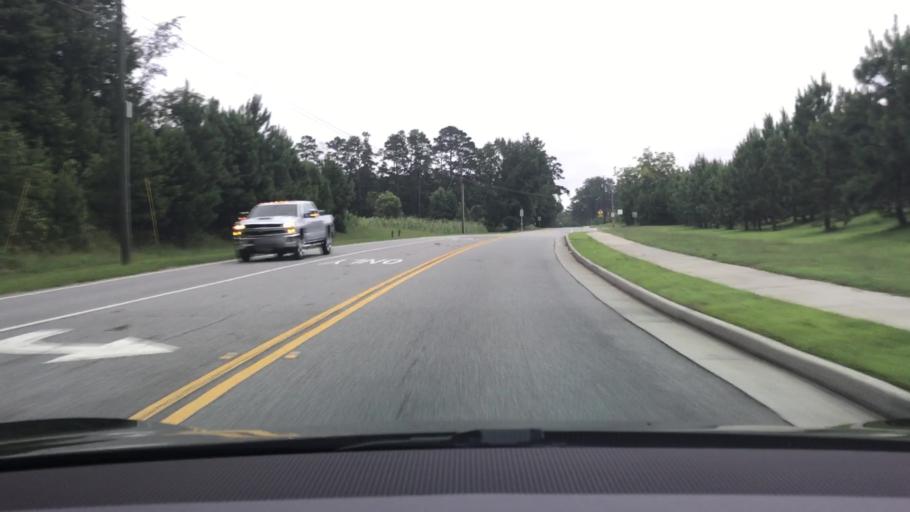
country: US
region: Georgia
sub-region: Gwinnett County
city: Suwanee
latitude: 34.0817
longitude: -84.0608
